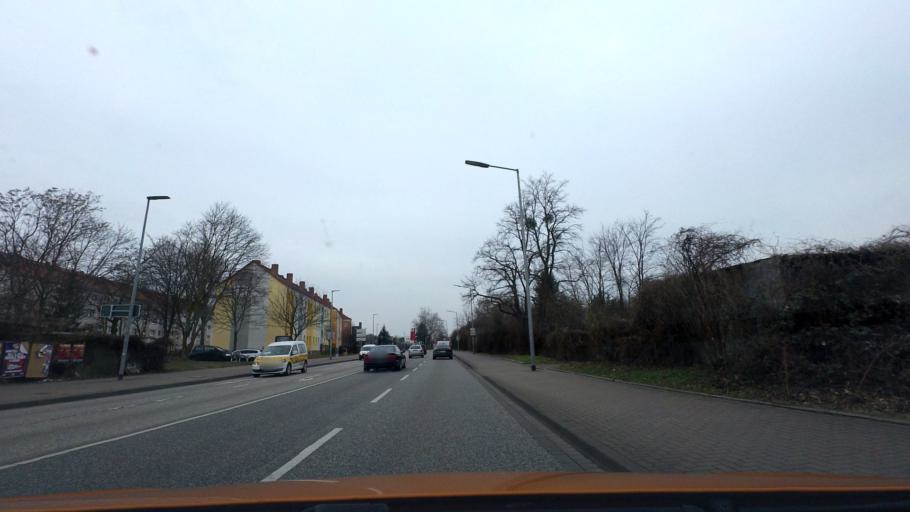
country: DE
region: Saxony-Anhalt
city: Neue Neustadt
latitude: 52.1410
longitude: 11.6265
